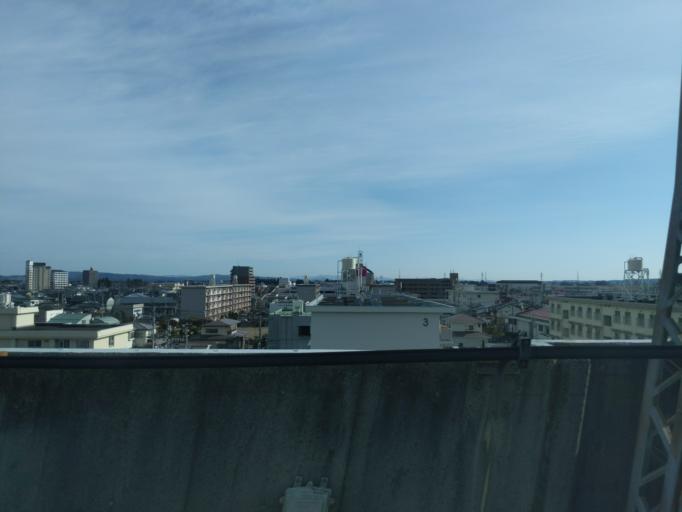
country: JP
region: Miyagi
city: Furukawa
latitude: 38.5682
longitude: 140.9673
